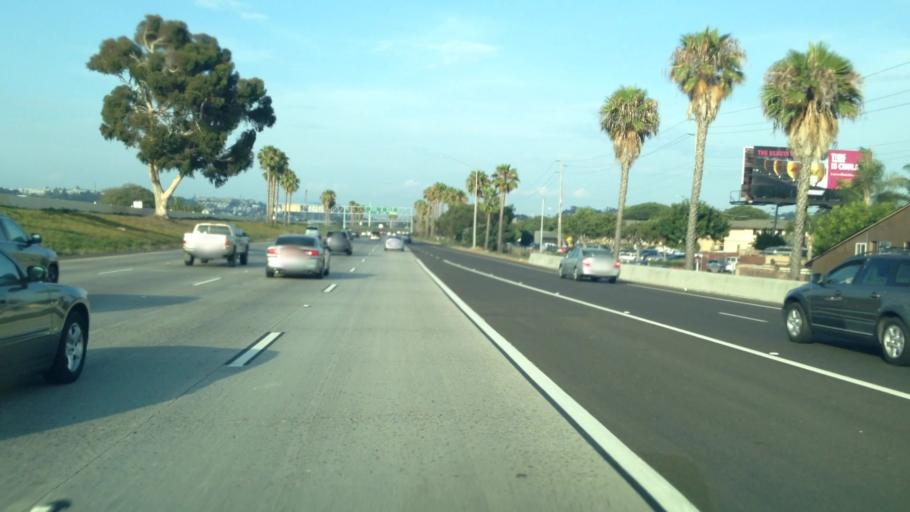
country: US
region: California
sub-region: San Diego County
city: San Diego
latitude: 32.7572
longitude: -117.2194
